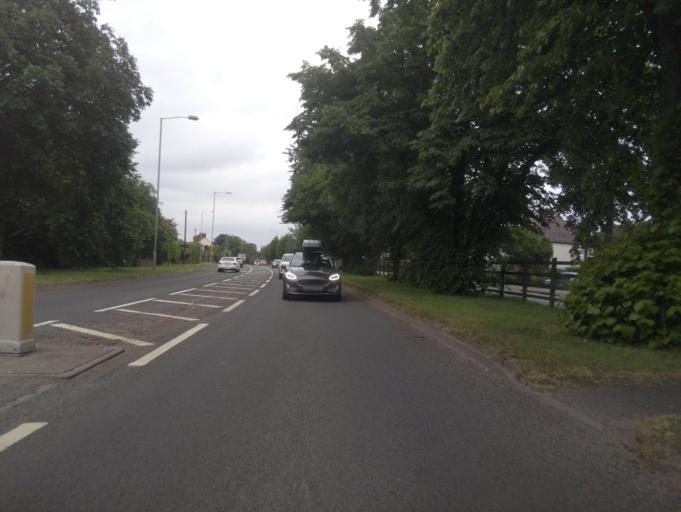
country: GB
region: England
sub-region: Staffordshire
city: Penkridge
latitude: 52.7195
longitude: -2.1174
